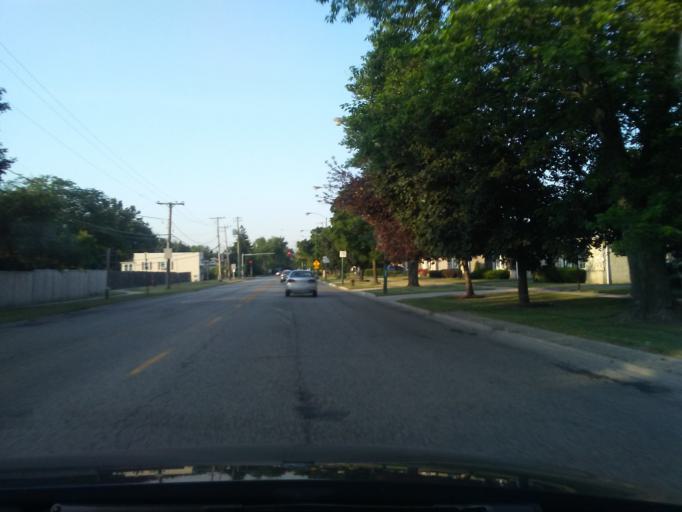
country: US
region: Illinois
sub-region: Cook County
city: Lincolnwood
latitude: 42.0063
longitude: -87.7618
